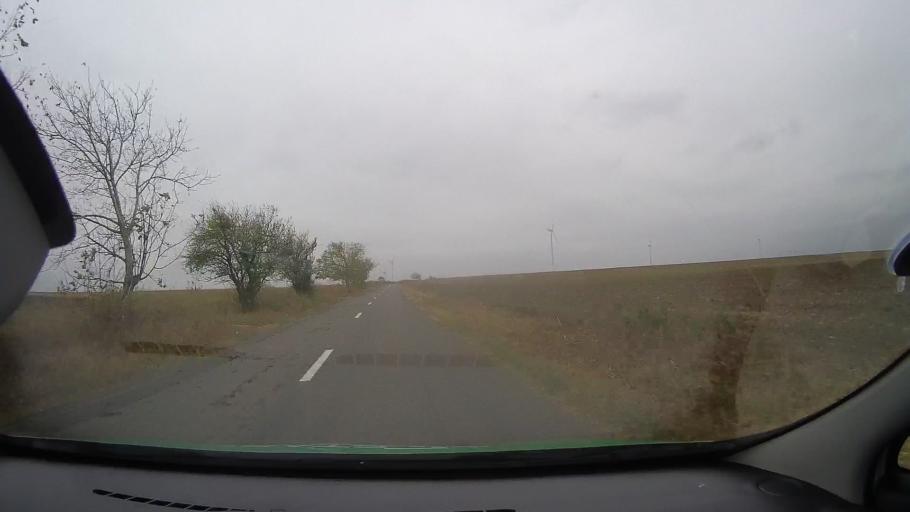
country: RO
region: Constanta
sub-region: Comuna Pantelimon
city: Pantelimon
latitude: 44.5010
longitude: 28.3550
